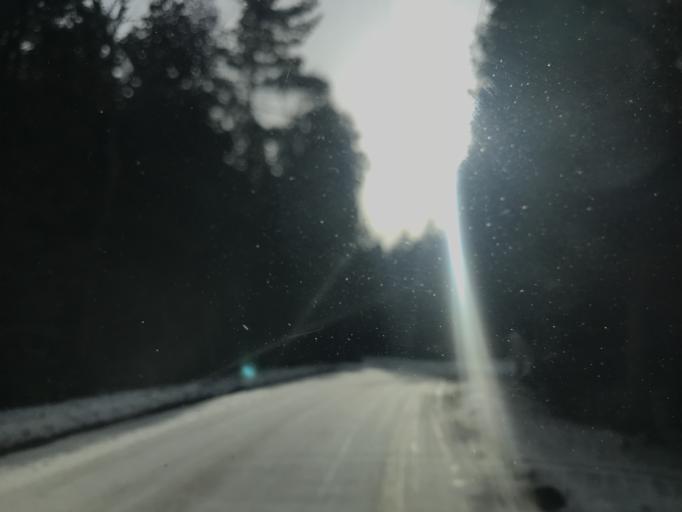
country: US
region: Wisconsin
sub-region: Door County
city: Sturgeon Bay
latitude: 45.1388
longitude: -87.0482
